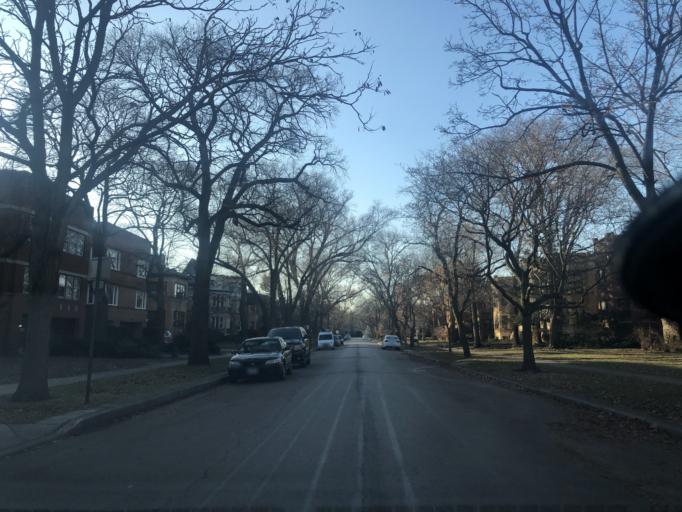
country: US
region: Illinois
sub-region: Cook County
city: Evanston
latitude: 42.0246
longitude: -87.6868
